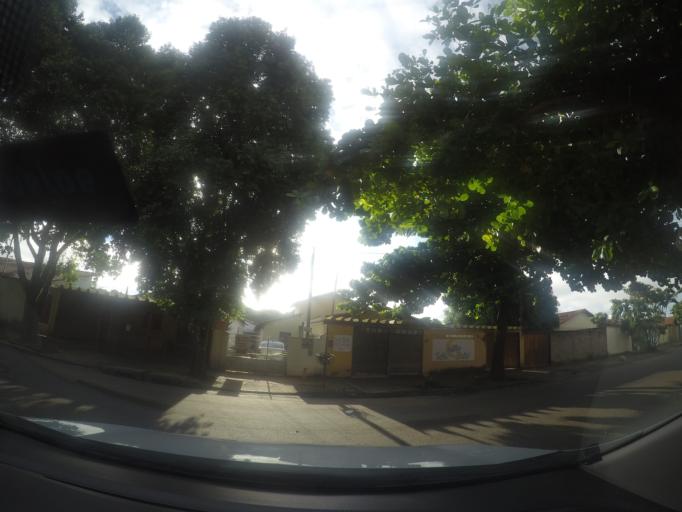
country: BR
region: Goias
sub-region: Goiania
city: Goiania
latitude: -16.6831
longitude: -49.3117
